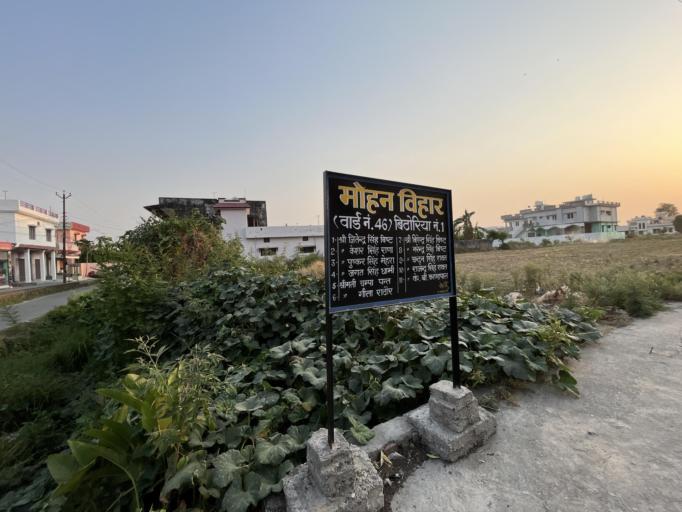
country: IN
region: Uttarakhand
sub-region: Naini Tal
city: Haldwani
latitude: 29.2284
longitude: 79.5096
